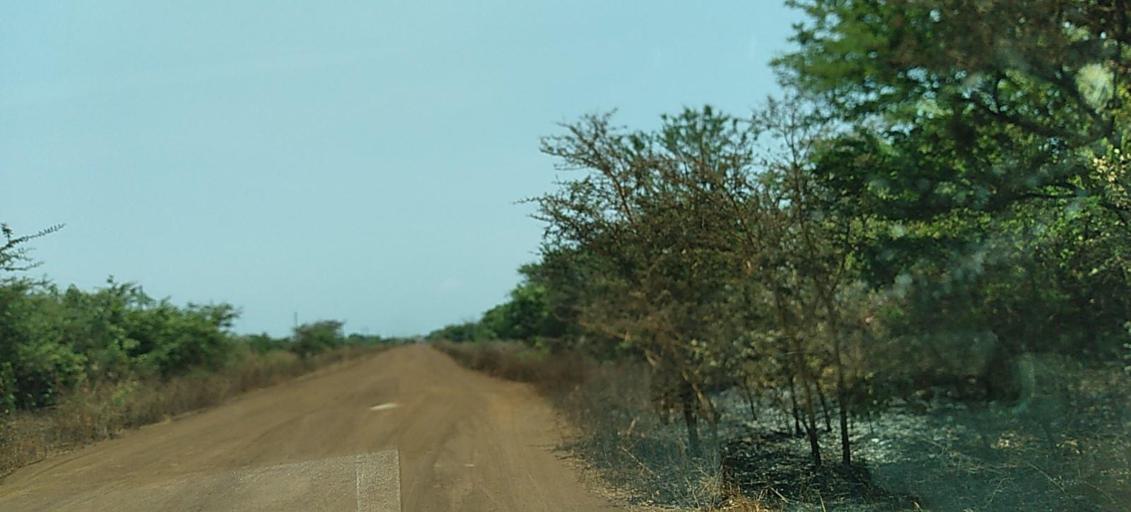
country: ZM
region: Copperbelt
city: Mpongwe
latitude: -13.7149
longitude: 27.8685
